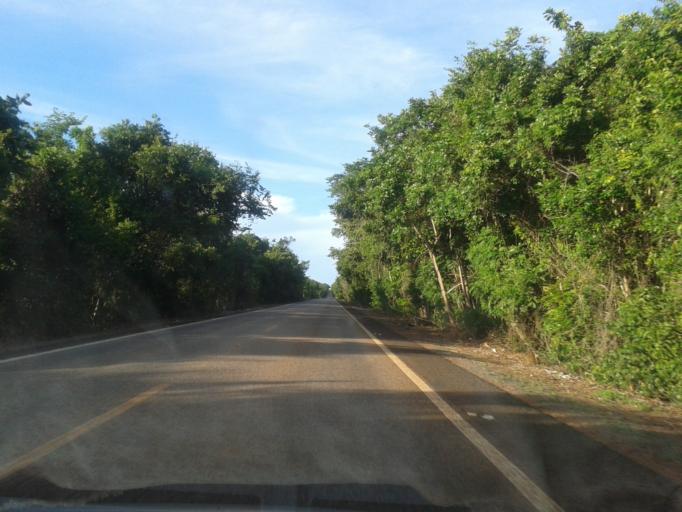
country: BR
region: Goias
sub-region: Sao Miguel Do Araguaia
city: Sao Miguel do Araguaia
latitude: -13.5202
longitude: -50.3031
